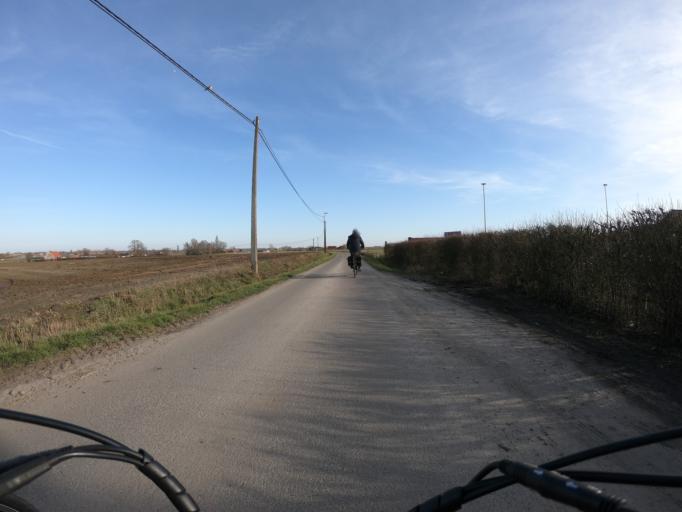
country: BE
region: Flanders
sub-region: Provincie West-Vlaanderen
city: Moorslede
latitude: 50.8804
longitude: 3.0755
